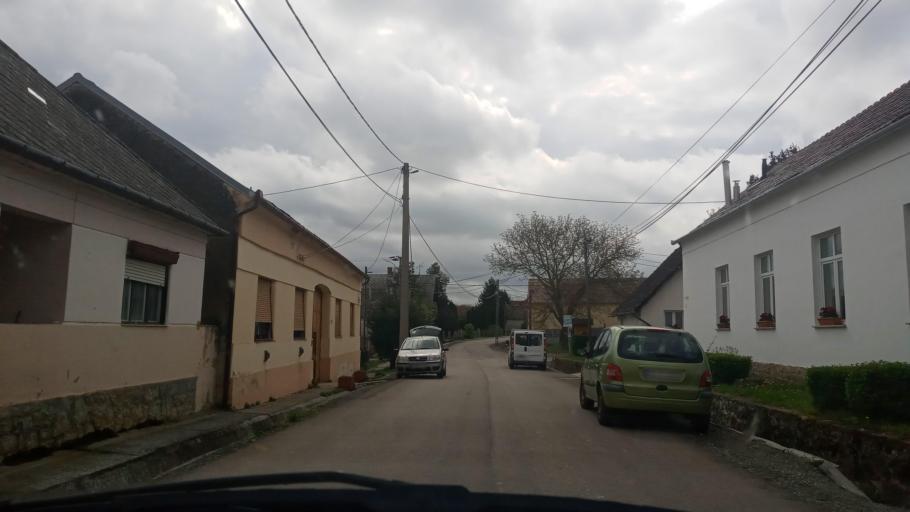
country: HU
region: Baranya
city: Boly
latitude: 45.9742
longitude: 18.4316
